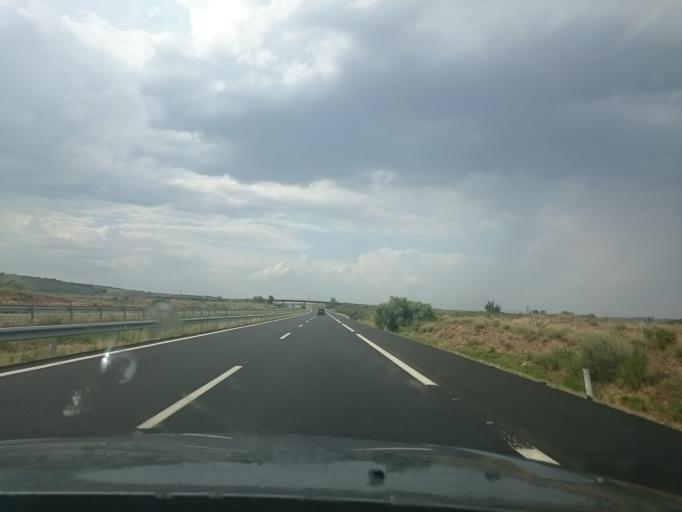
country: ES
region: Navarre
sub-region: Provincia de Navarra
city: Azagra
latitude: 42.2635
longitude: -1.9261
